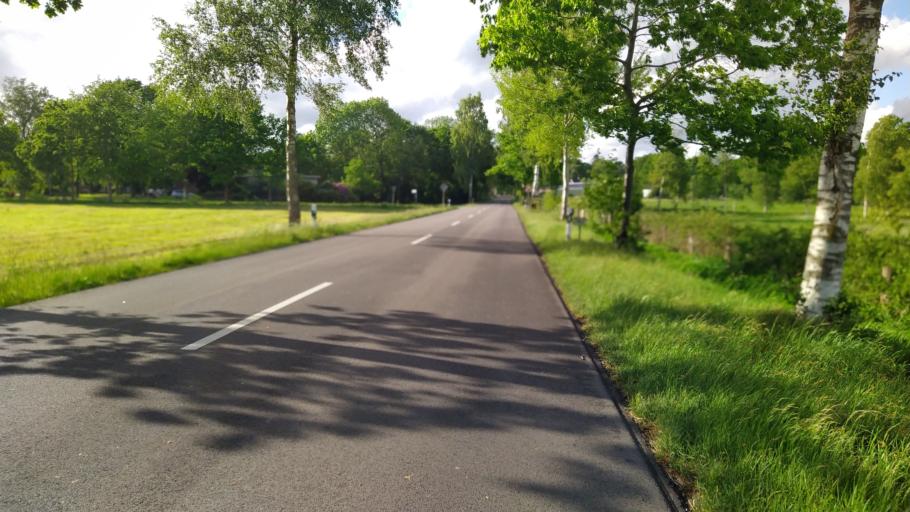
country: DE
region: Lower Saxony
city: Farven
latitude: 53.4431
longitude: 9.3209
